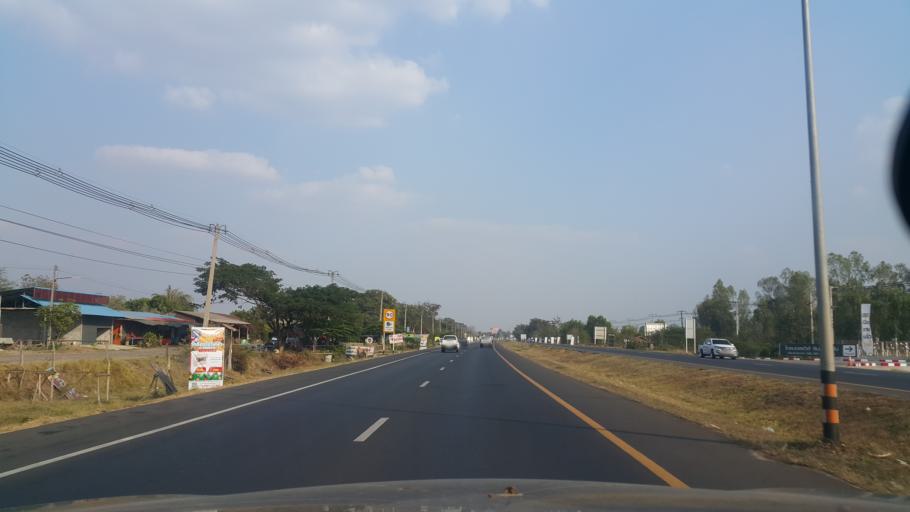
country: TH
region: Buriram
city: Nang Rong
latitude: 14.6313
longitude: 102.8318
